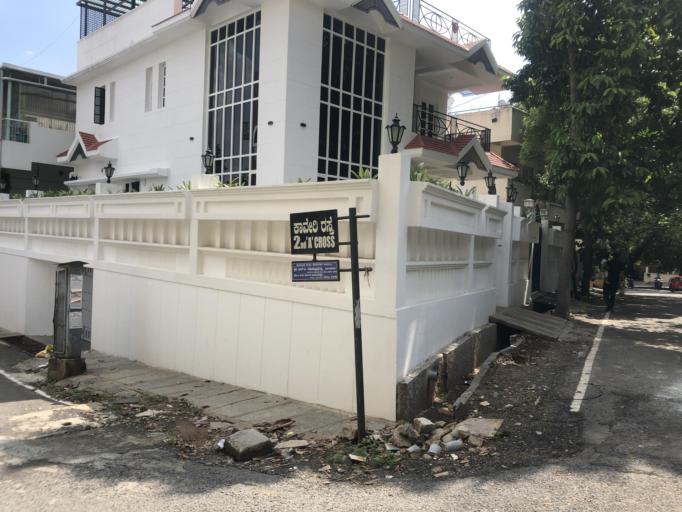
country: IN
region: Karnataka
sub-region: Bangalore Urban
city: Bangalore
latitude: 12.9375
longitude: 77.5473
